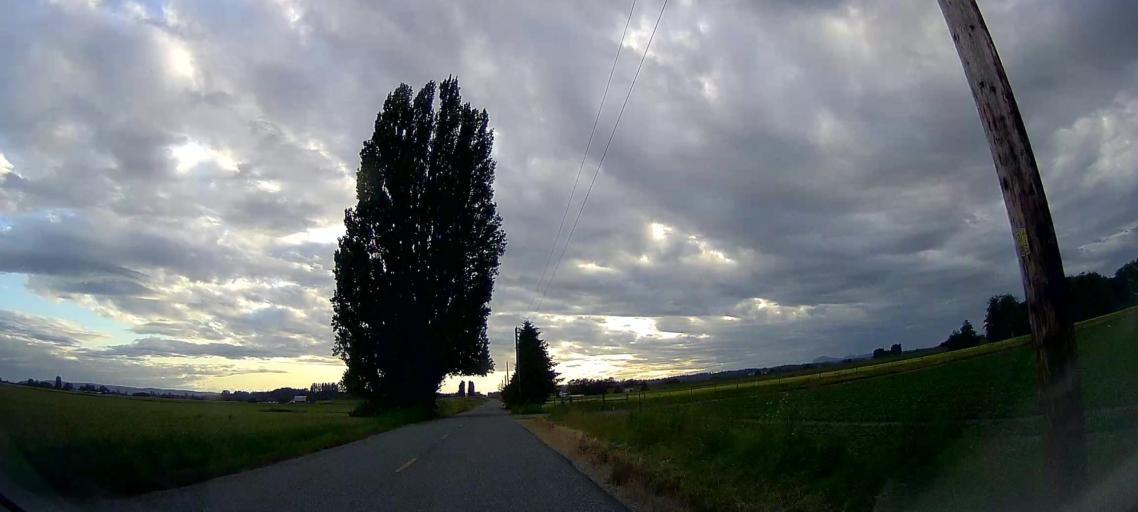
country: US
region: Washington
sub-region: Skagit County
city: Mount Vernon
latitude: 48.3702
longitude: -122.3866
